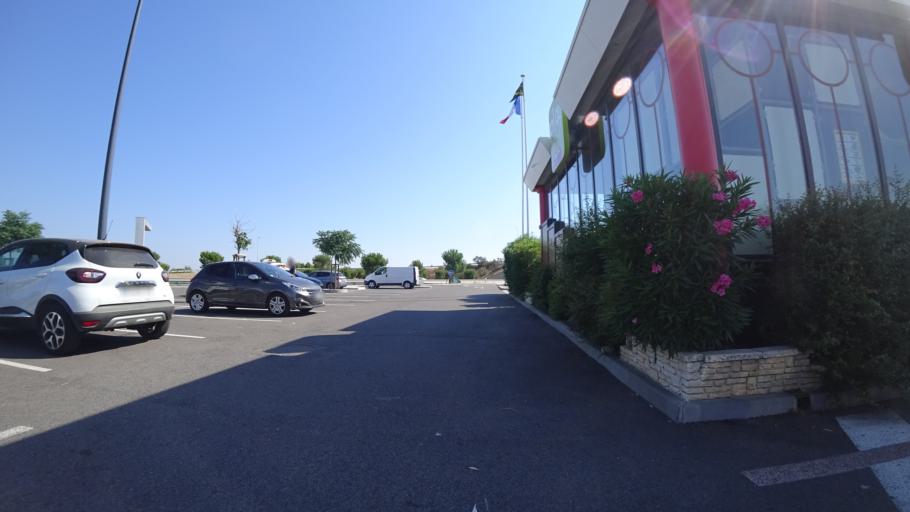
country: FR
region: Languedoc-Roussillon
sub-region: Departement des Pyrenees-Orientales
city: Pia
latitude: 42.7769
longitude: 2.9147
